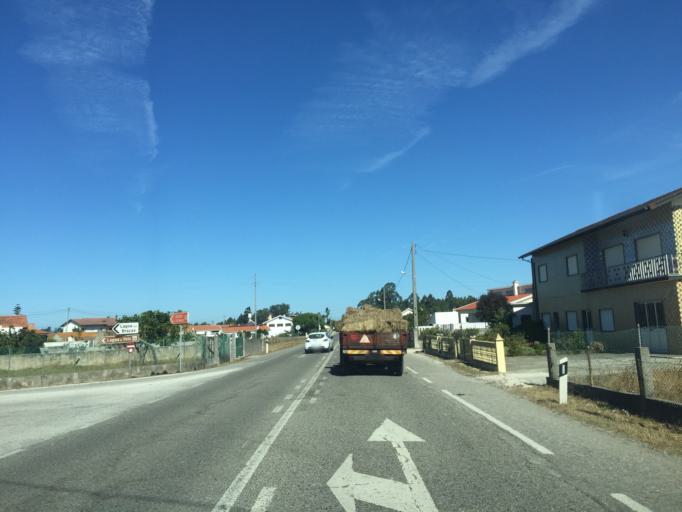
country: PT
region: Coimbra
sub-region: Figueira da Foz
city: Alhadas
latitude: 40.2429
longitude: -8.7906
